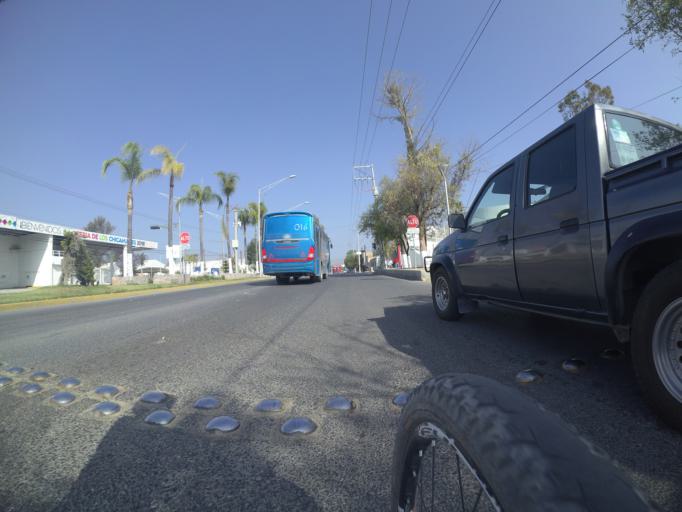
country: MX
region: Aguascalientes
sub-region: Jesus Maria
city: Jesus Maria
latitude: 21.9565
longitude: -102.3397
